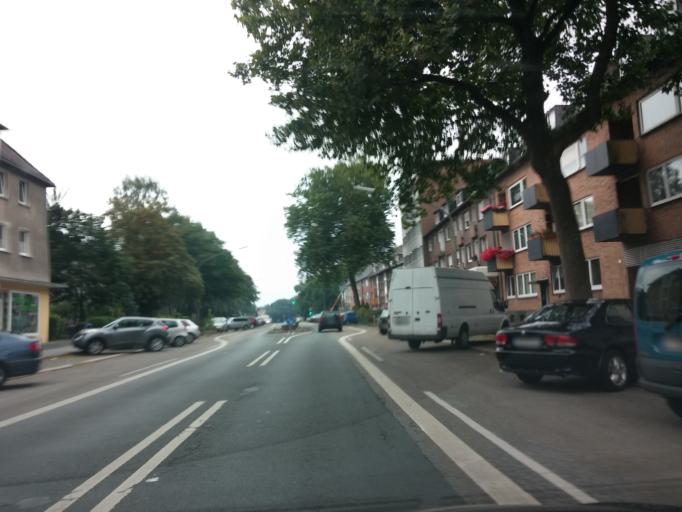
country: DE
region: North Rhine-Westphalia
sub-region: Regierungsbezirk Munster
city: Gladbeck
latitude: 51.5938
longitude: 7.0518
